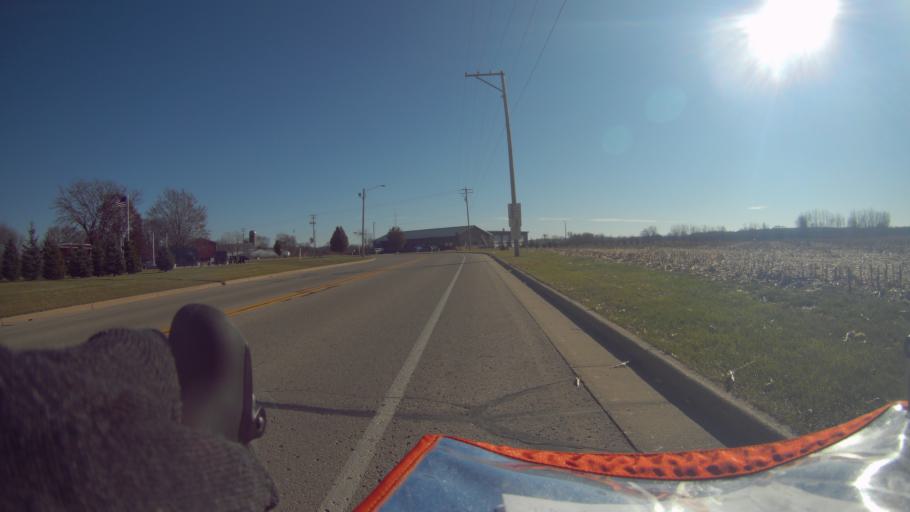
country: US
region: Wisconsin
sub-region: Green County
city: Brooklyn
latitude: 42.8541
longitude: -89.3801
